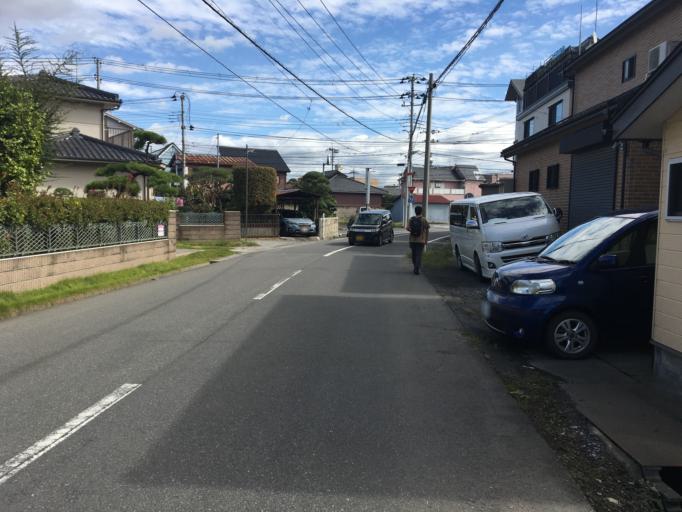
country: JP
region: Saitama
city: Gyoda
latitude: 36.1409
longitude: 139.4554
